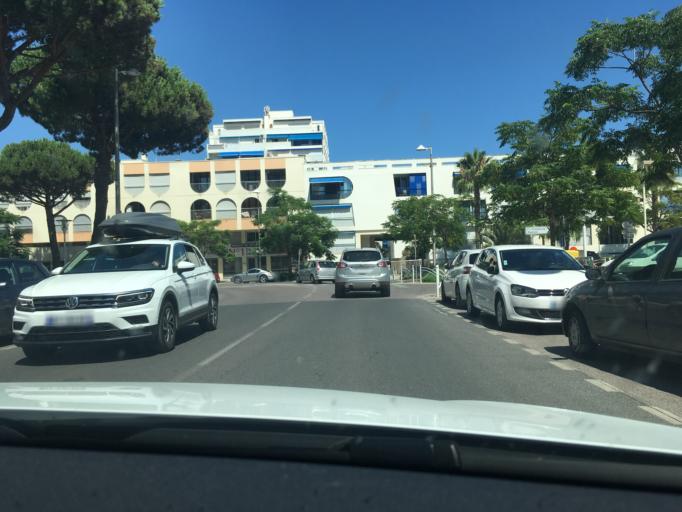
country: FR
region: Languedoc-Roussillon
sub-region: Departement de l'Herault
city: La Grande-Motte
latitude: 43.5582
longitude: 4.0880
